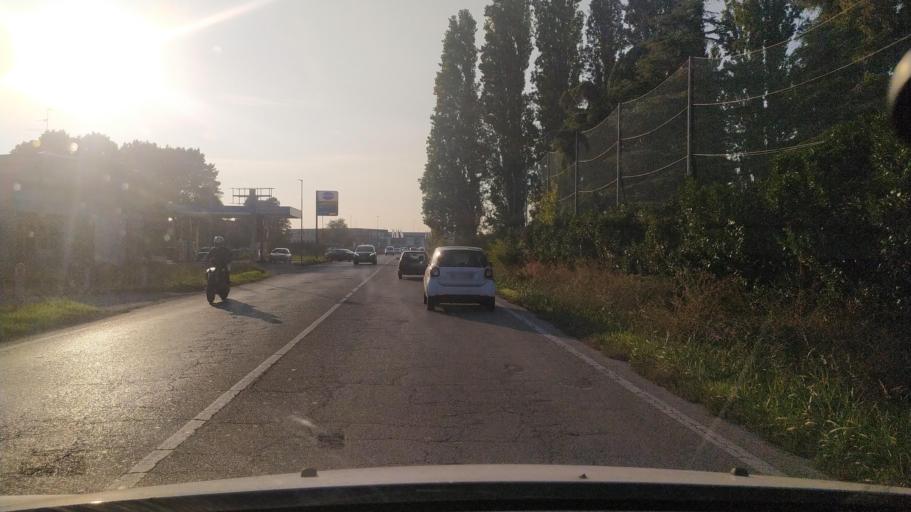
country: IT
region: Lombardy
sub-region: Provincia di Cremona
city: Capergnanica
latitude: 45.3595
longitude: 9.6472
